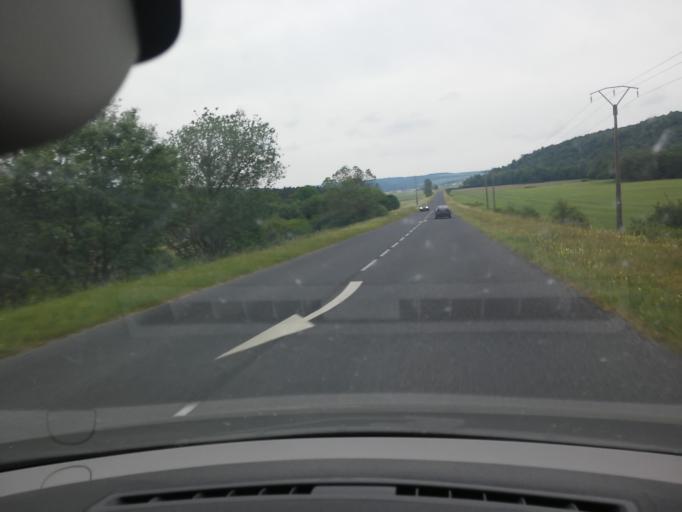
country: FR
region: Lorraine
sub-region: Departement de la Meuse
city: Saint-Mihiel
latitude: 48.9000
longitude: 5.4635
